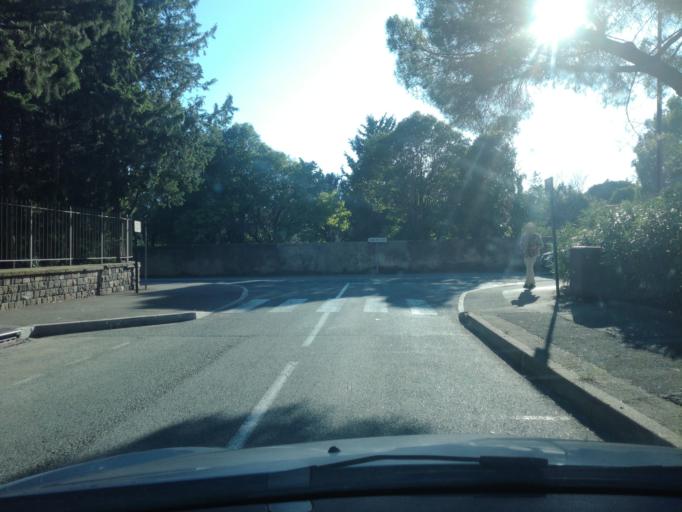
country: FR
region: Provence-Alpes-Cote d'Azur
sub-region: Departement du Var
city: Frejus
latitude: 43.4375
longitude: 6.7377
